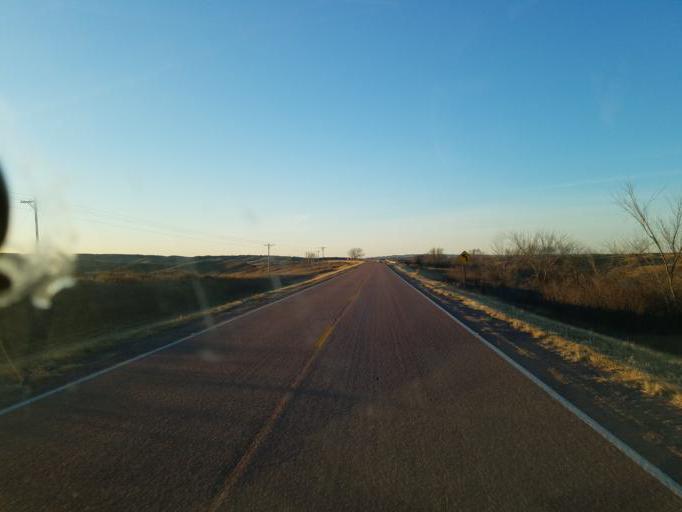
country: US
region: South Dakota
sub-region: Bon Homme County
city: Springfield
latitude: 42.7397
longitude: -97.9119
